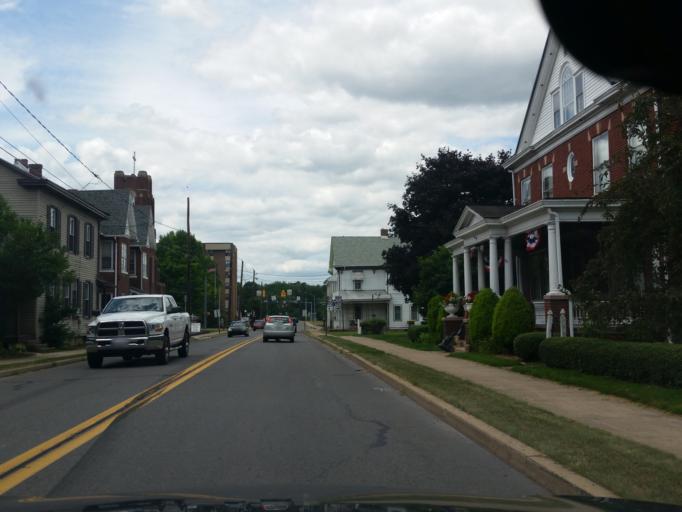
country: US
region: Pennsylvania
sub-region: Northumberland County
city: Milton
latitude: 41.0149
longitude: -76.8544
